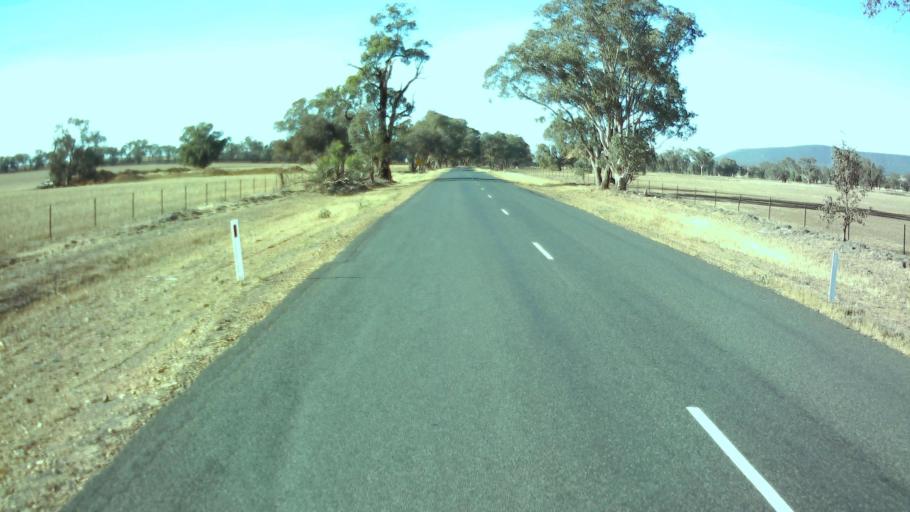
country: AU
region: New South Wales
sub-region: Weddin
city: Grenfell
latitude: -33.9357
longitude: 148.1377
